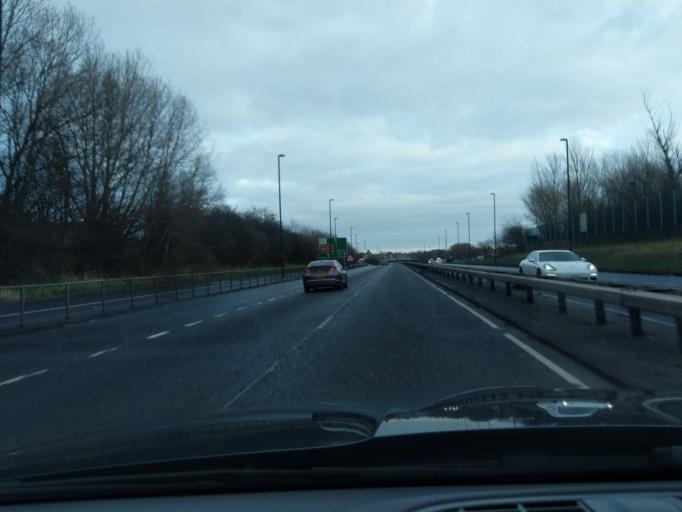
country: GB
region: England
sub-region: Borough of North Tyneside
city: Wallsend
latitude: 54.9980
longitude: -1.5515
